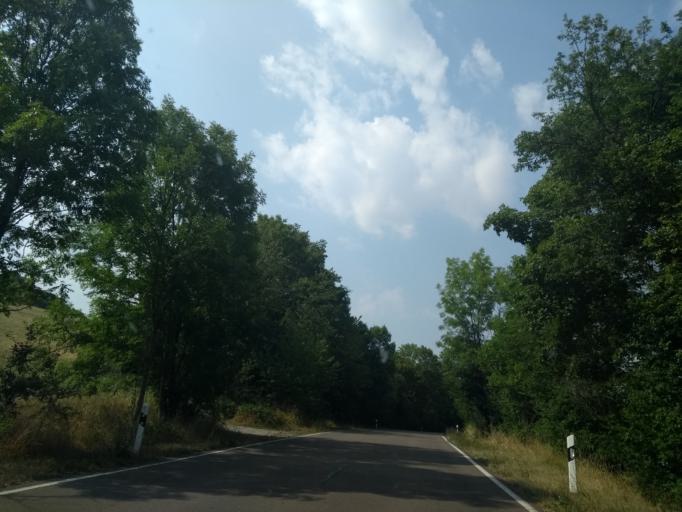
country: DE
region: Saxony-Anhalt
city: Kretzschau
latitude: 51.0278
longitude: 12.0970
